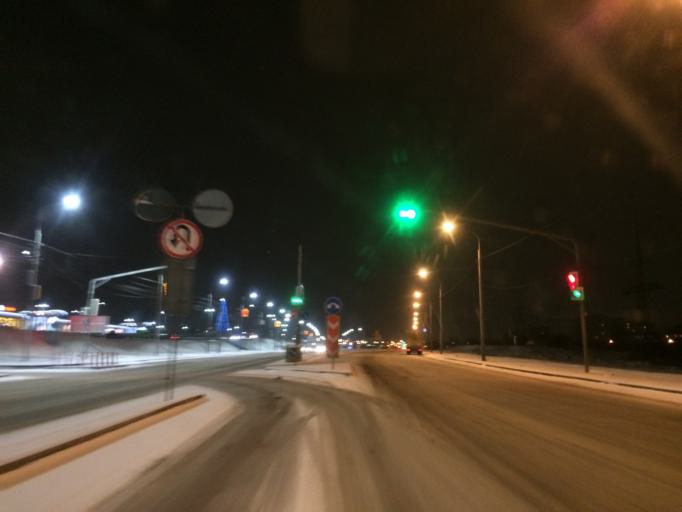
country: RU
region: Tula
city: Tula
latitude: 54.1796
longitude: 37.6472
